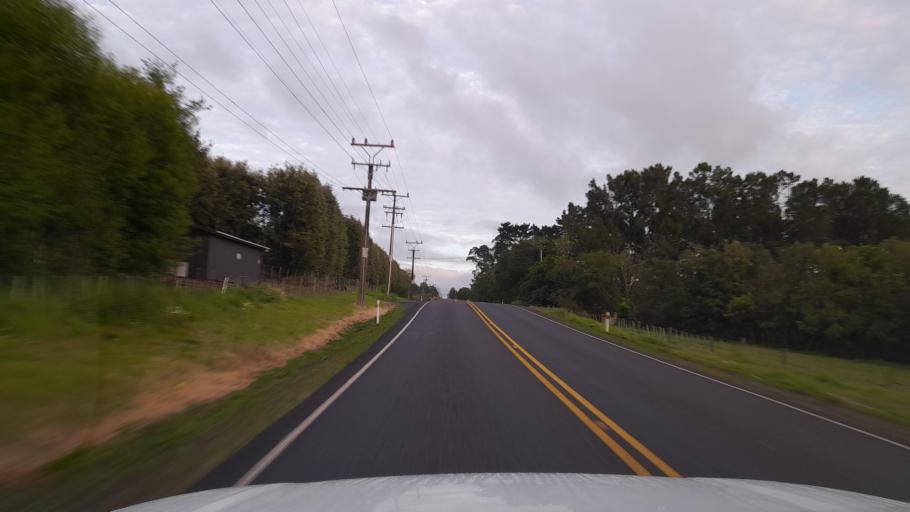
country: NZ
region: Northland
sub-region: Whangarei
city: Maungatapere
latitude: -35.7529
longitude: 174.1718
